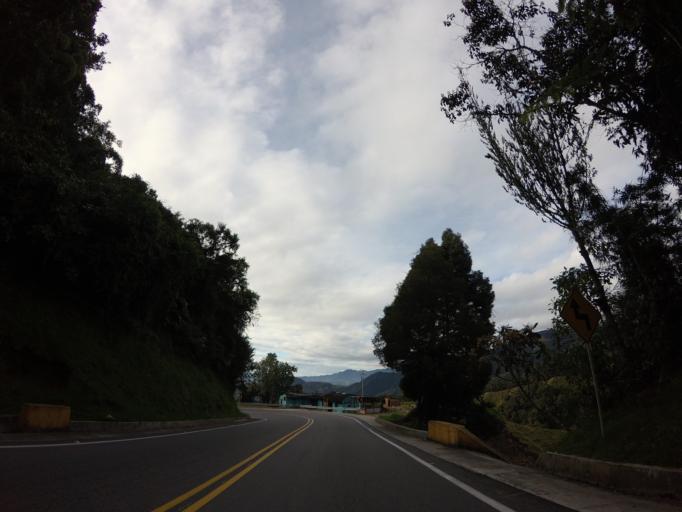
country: CO
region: Tolima
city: Herveo
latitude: 5.1069
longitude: -75.2613
